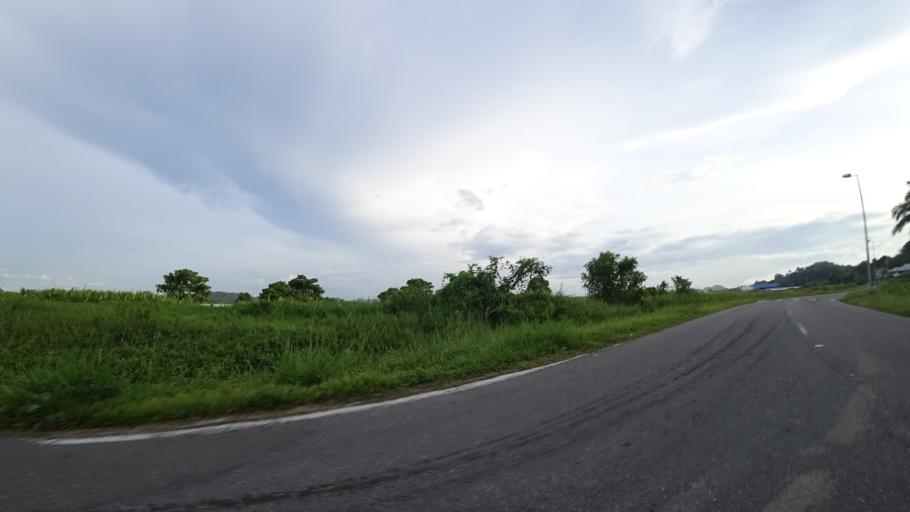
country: BN
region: Brunei and Muara
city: Bandar Seri Begawan
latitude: 4.8388
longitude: 114.8216
